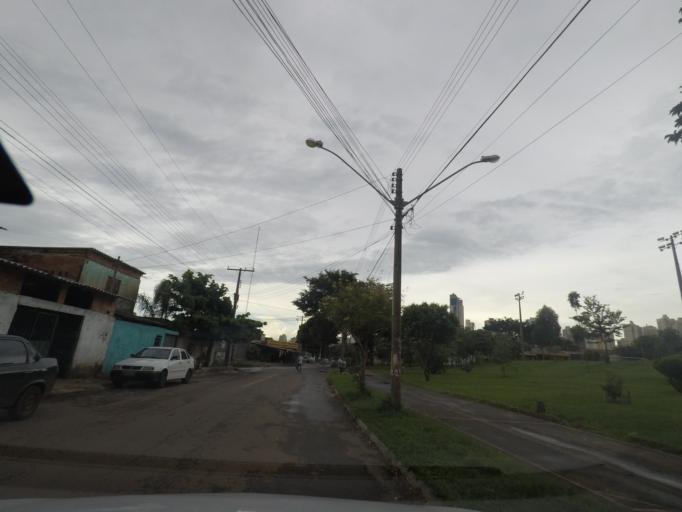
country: BR
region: Goias
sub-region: Goiania
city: Goiania
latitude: -16.7185
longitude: -49.2455
